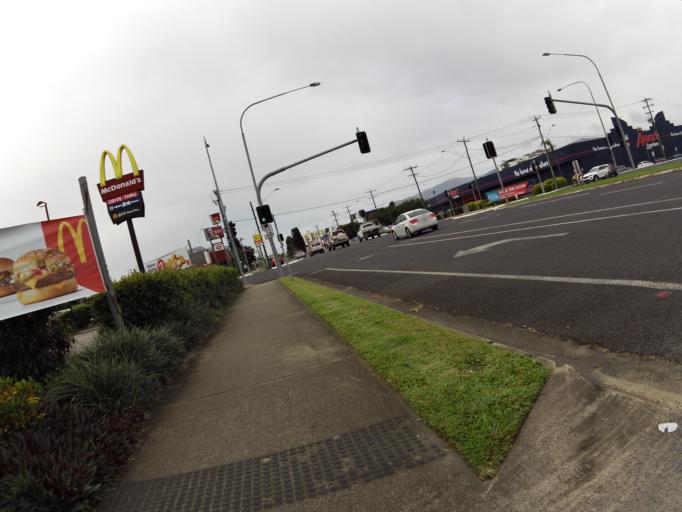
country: AU
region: Queensland
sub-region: Cairns
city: Cairns
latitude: -16.9232
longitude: 145.7670
